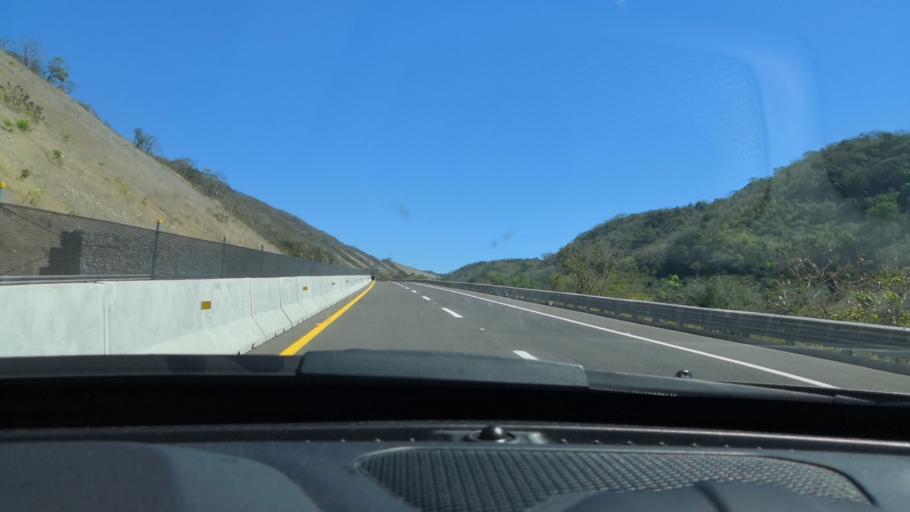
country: MX
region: Nayarit
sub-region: Compostela
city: Juan Escutia (Borbollon)
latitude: 21.1317
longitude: -104.9051
